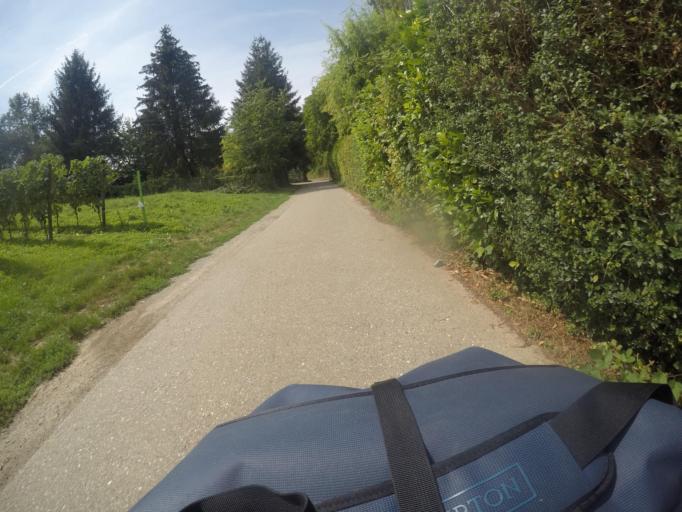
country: DE
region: Baden-Wuerttemberg
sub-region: Freiburg Region
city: Ebringen
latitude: 47.9746
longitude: 7.7889
